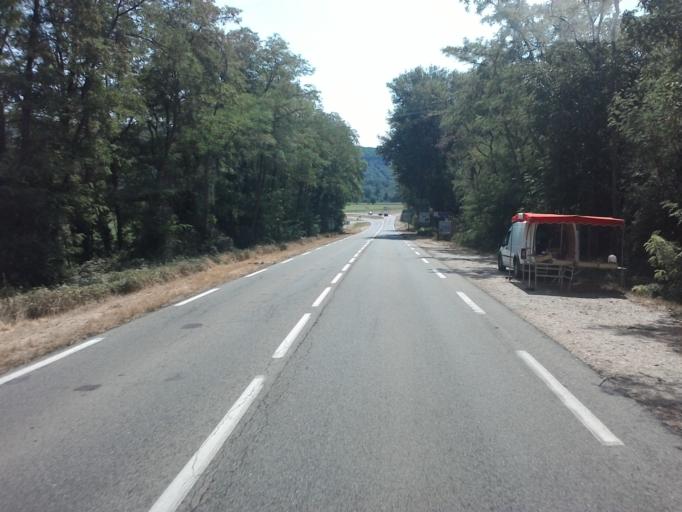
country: FR
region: Rhone-Alpes
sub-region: Departement de l'Ain
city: Lagnieu
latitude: 45.8814
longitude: 5.3476
